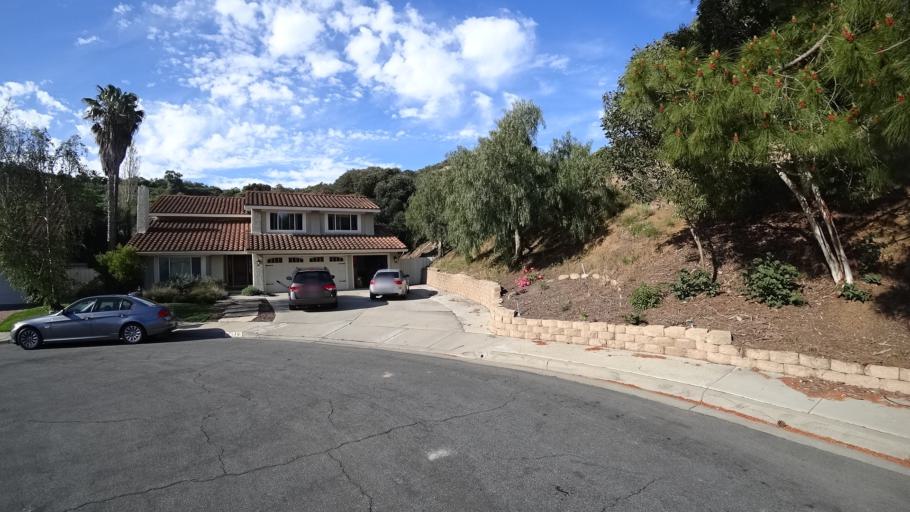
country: US
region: California
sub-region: Ventura County
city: Casa Conejo
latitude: 34.1684
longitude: -118.9497
